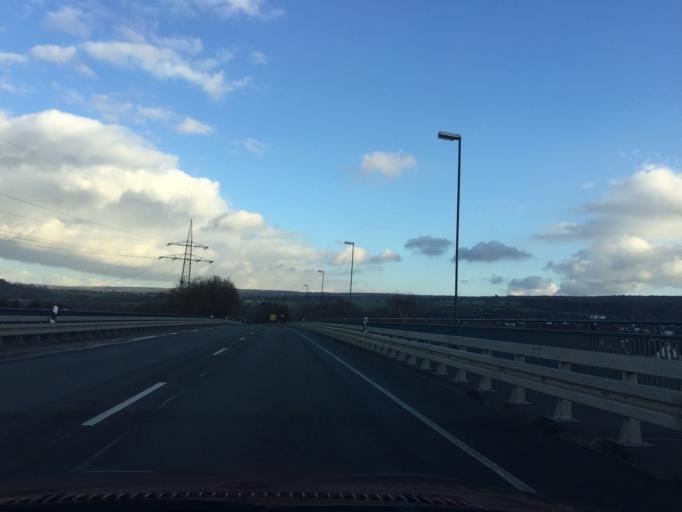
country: DE
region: Lower Saxony
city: Holzminden
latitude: 51.7984
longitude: 9.4207
